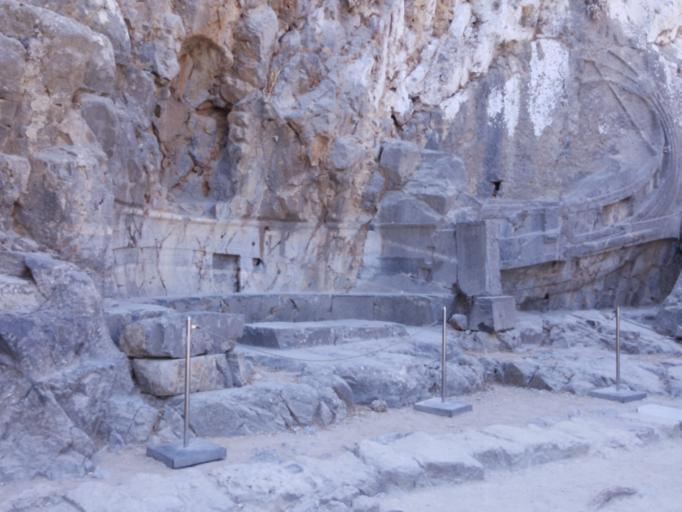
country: GR
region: South Aegean
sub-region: Nomos Dodekanisou
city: Lardos
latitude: 36.0920
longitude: 28.0888
